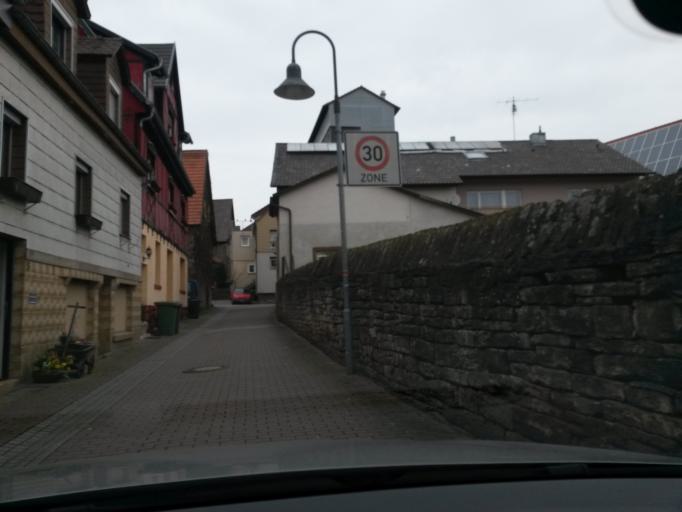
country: DE
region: Baden-Wuerttemberg
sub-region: Karlsruhe Region
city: Neuenburg
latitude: 48.8877
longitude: 8.5465
